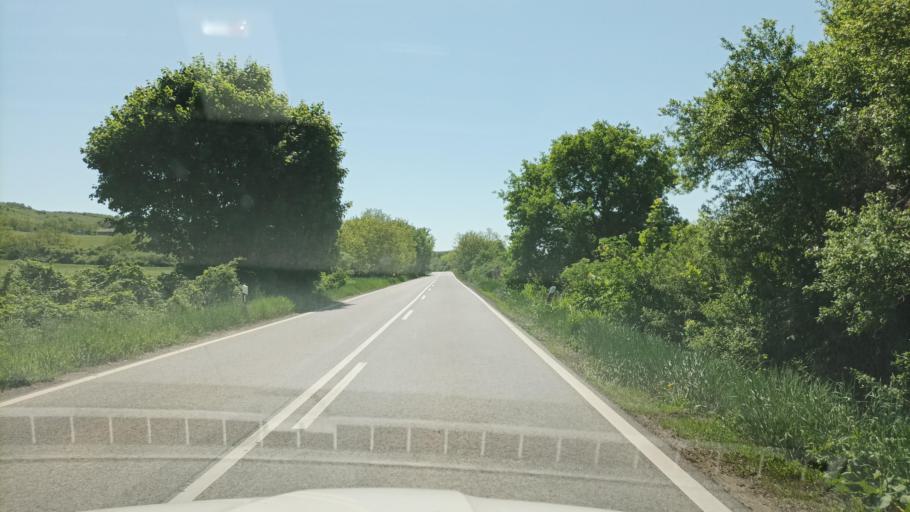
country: HU
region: Pest
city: Acsa
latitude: 47.7520
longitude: 19.3684
